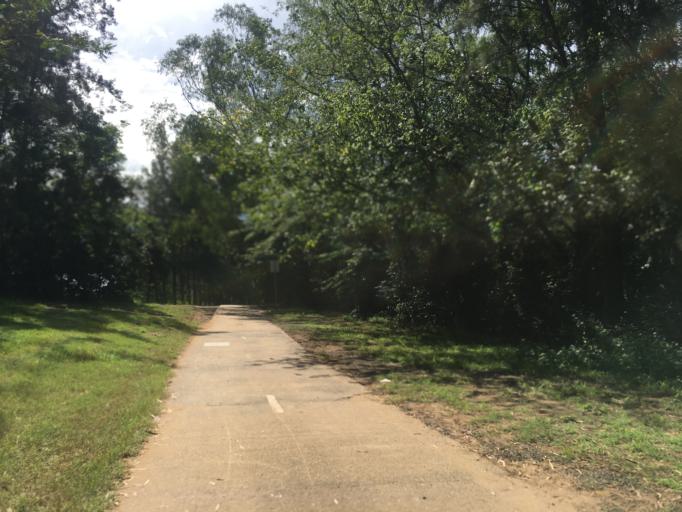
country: AU
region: New South Wales
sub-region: Camden
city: Elderslie
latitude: -34.0653
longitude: 150.6993
